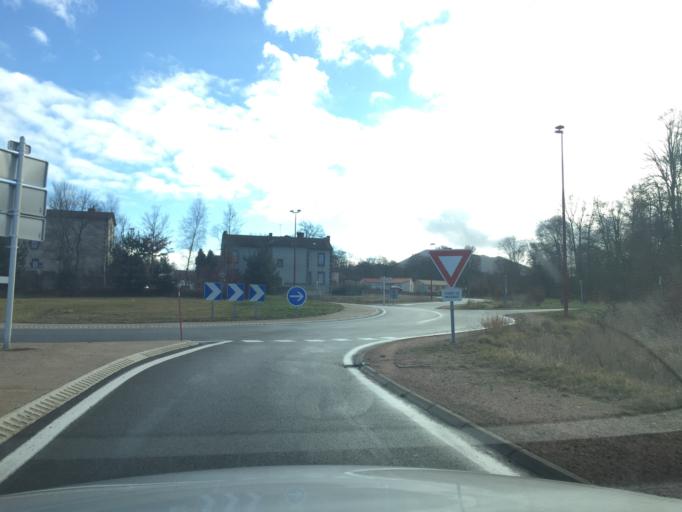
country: FR
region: Auvergne
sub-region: Departement du Puy-de-Dome
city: Saint-Ours
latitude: 45.8244
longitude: 2.9114
